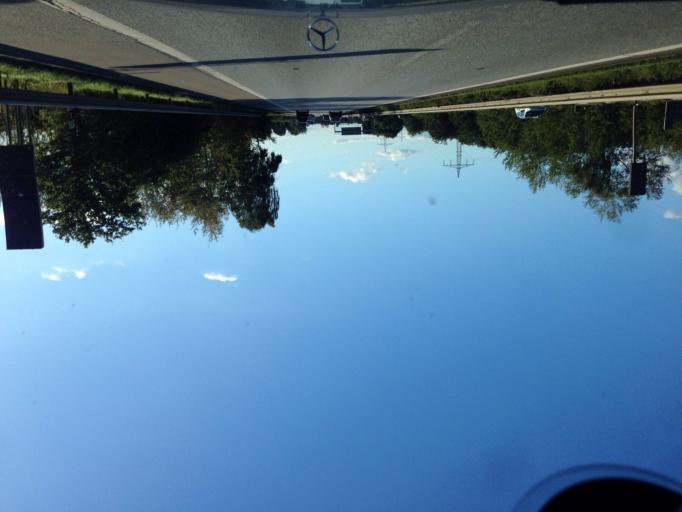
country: DE
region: Schleswig-Holstein
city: Padenstedt
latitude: 54.0683
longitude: 9.9225
